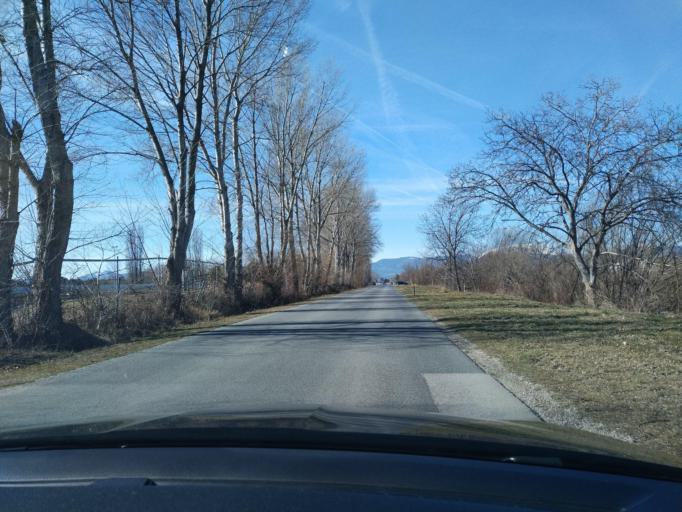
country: AT
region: Lower Austria
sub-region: Politischer Bezirk Neunkirchen
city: Breitenau
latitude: 47.7202
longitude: 16.1332
